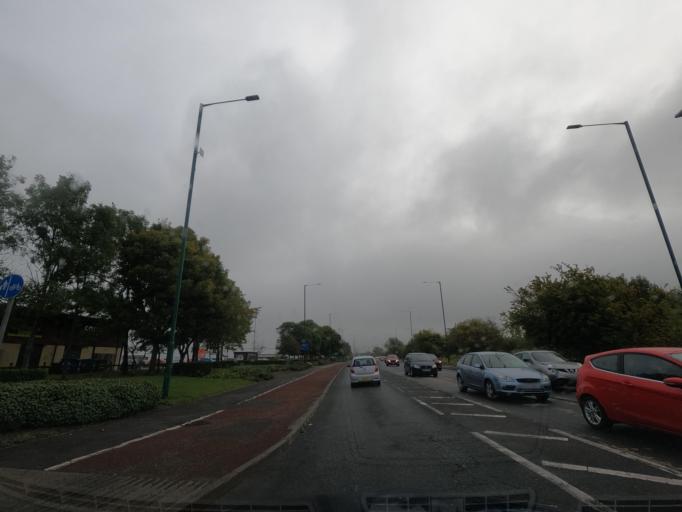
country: GB
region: England
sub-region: Redcar and Cleveland
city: South Bank
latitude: 54.5700
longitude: -1.1816
